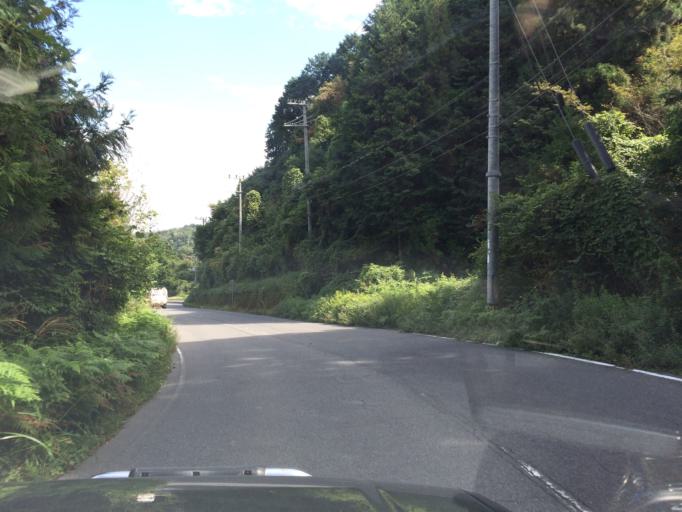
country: JP
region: Mie
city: Nabari
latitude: 34.6813
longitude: 136.0083
